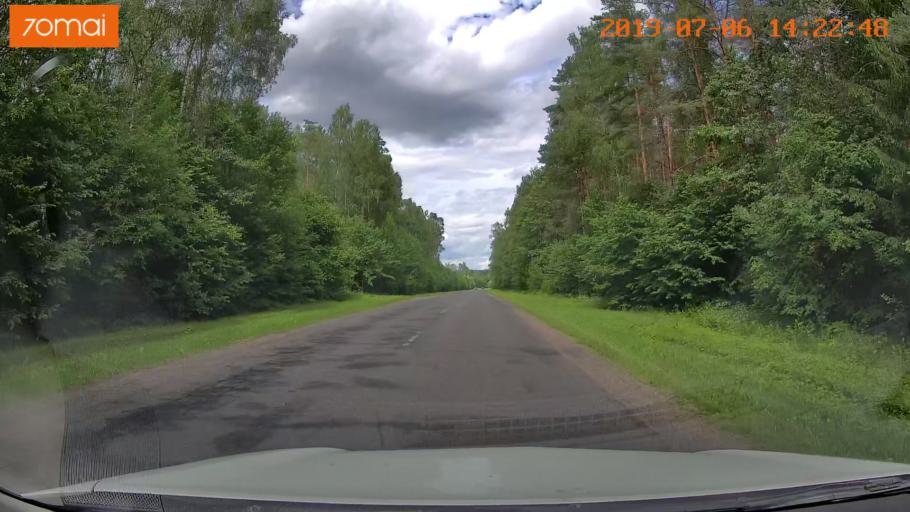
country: BY
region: Minsk
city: Ivyanyets
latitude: 53.9126
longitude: 26.7655
